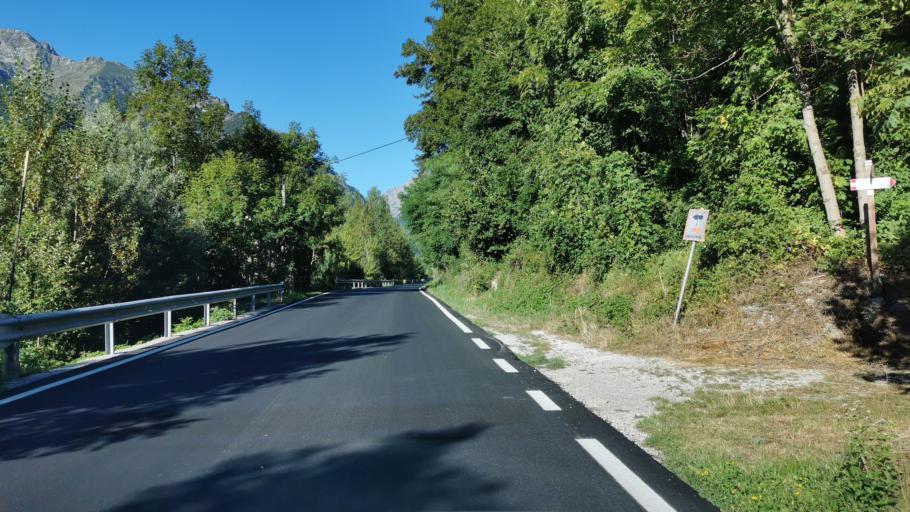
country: IT
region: Piedmont
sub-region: Provincia di Cuneo
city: Valdieri
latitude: 44.2637
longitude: 7.3794
